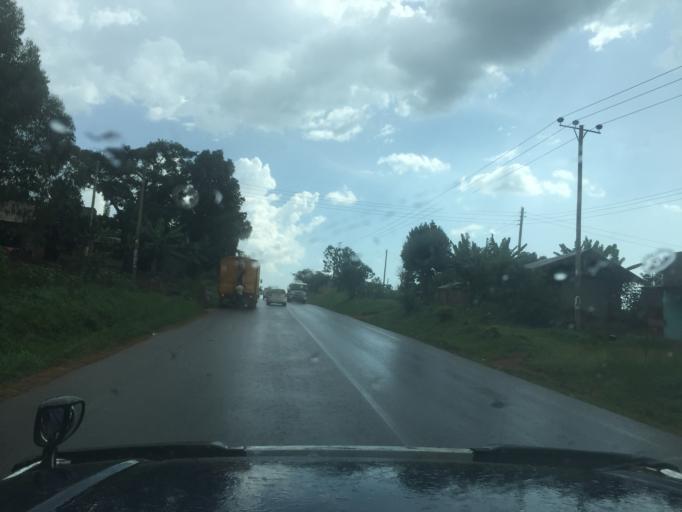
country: UG
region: Central Region
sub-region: Luwero District
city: Wobulenzi
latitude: 0.5698
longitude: 32.5304
